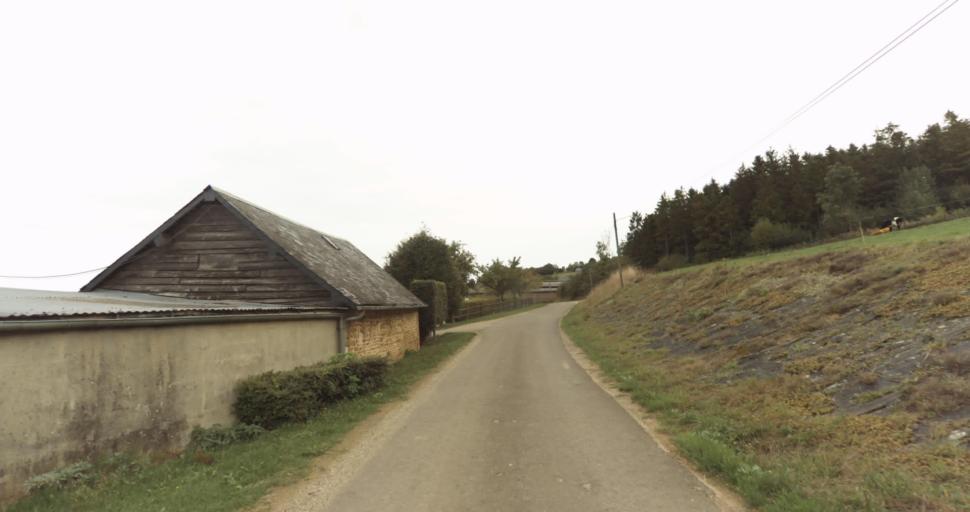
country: FR
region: Lower Normandy
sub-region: Departement de l'Orne
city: Gace
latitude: 48.7578
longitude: 0.3363
